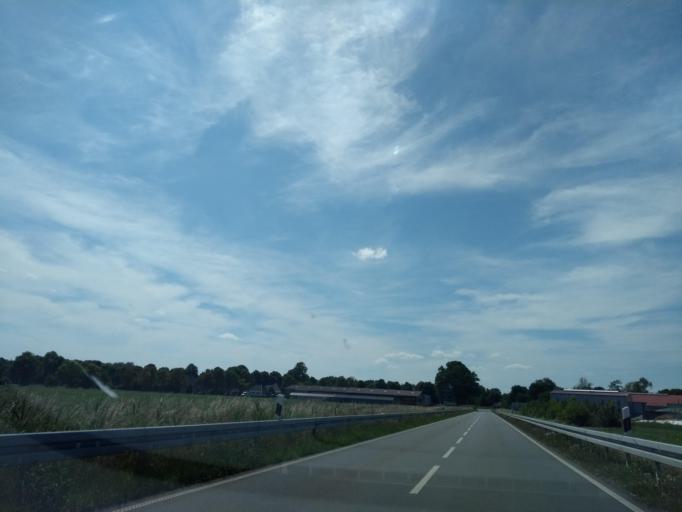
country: DE
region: Lower Saxony
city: Barenburg
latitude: 52.6255
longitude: 8.8063
